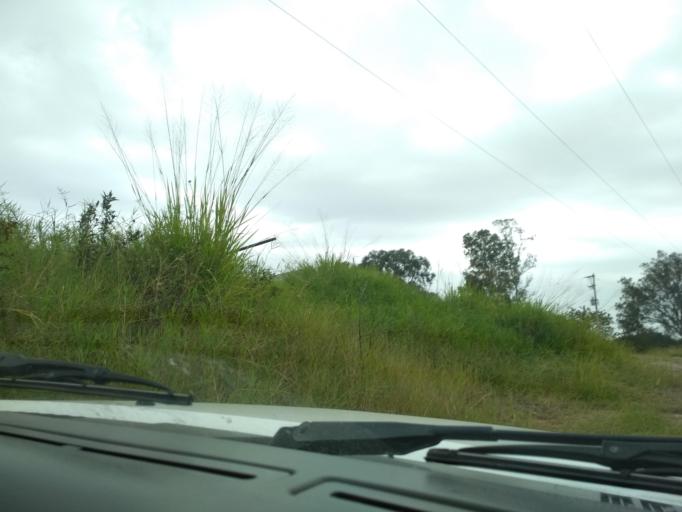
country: MX
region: Veracruz
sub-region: Emiliano Zapata
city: Dos Rios
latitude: 19.5189
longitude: -96.7935
